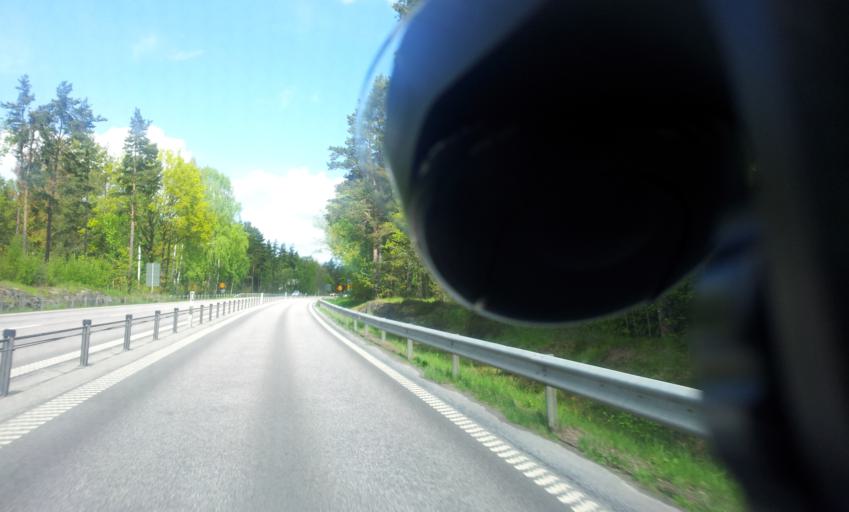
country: SE
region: Kalmar
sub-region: Oskarshamns Kommun
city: Oskarshamn
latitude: 57.3317
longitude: 16.4785
